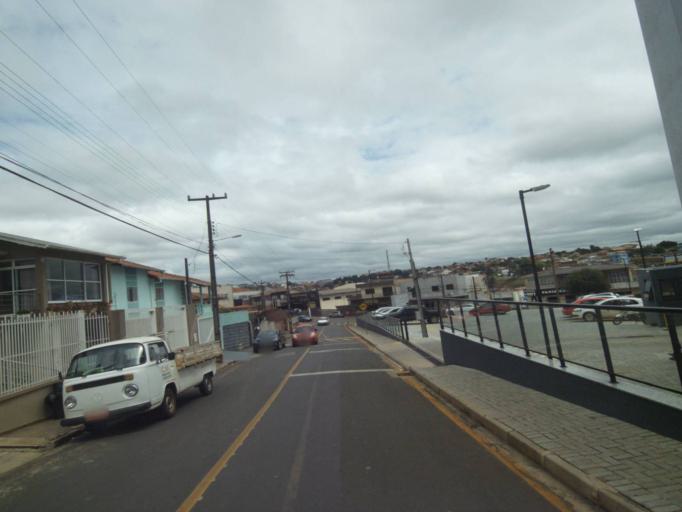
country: BR
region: Parana
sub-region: Telemaco Borba
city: Telemaco Borba
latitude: -24.3342
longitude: -50.6372
